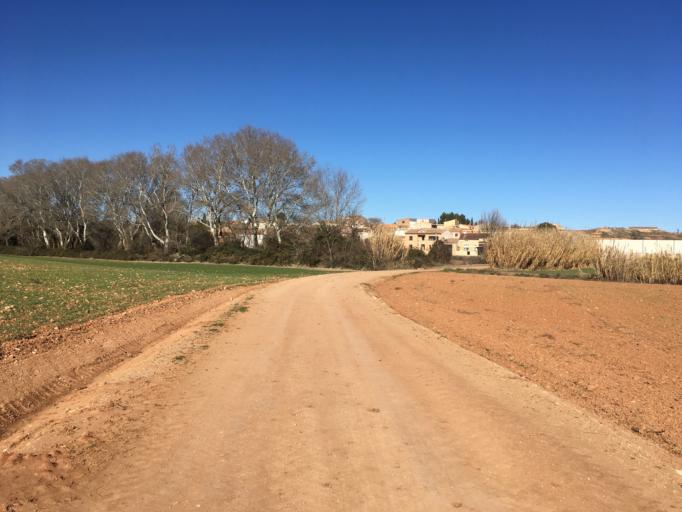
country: ES
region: Castille-La Mancha
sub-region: Provincia de Cuenca
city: Atalaya del Canavate
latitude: 39.5458
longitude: -2.2470
